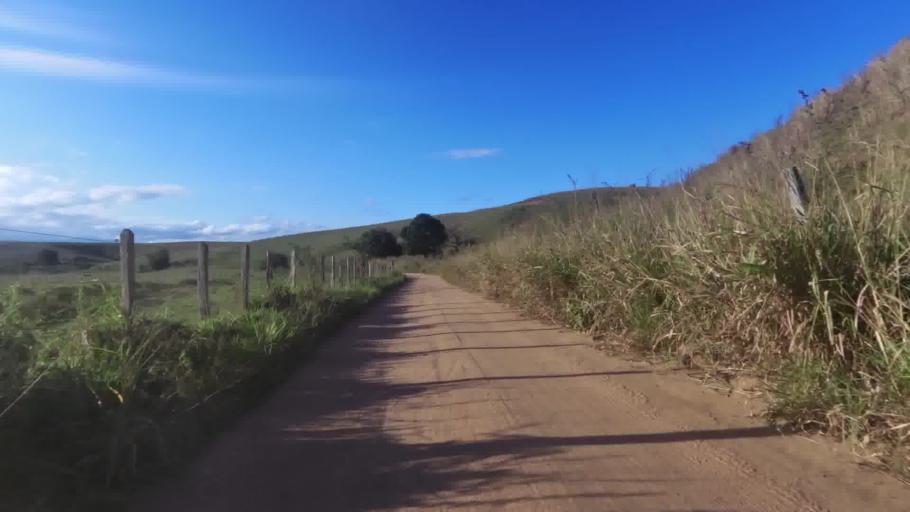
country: BR
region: Espirito Santo
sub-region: Marataizes
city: Marataizes
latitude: -21.1385
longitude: -41.0181
